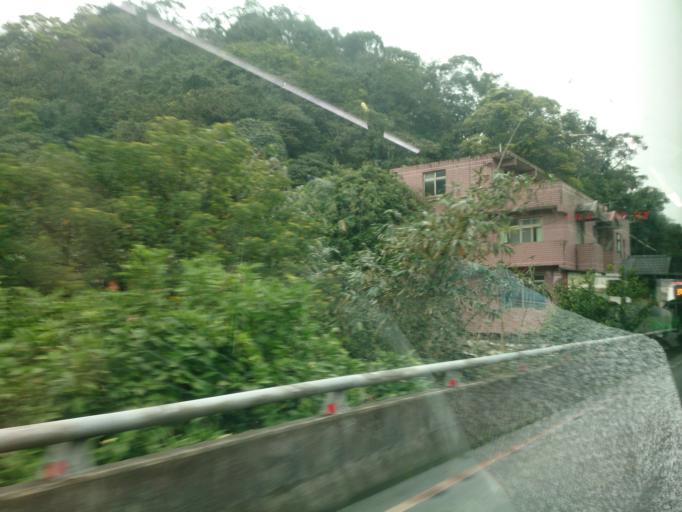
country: TW
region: Taiwan
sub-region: Keelung
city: Keelung
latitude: 25.0208
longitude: 121.7141
